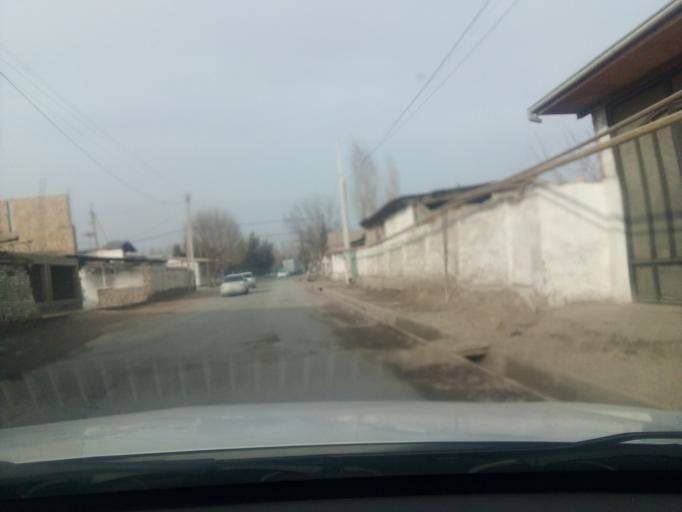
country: UZ
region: Namangan
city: Pop Shahri
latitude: 41.0005
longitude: 71.0936
